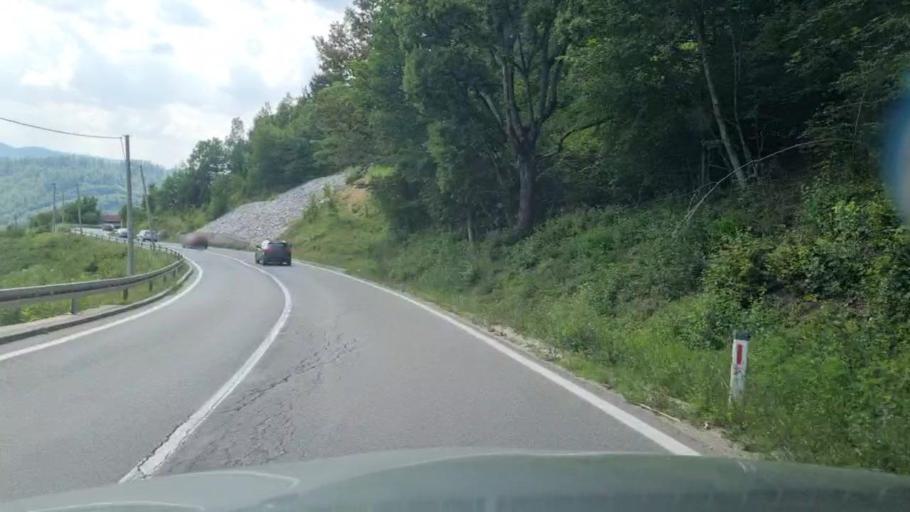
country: BA
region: Federation of Bosnia and Herzegovina
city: Kladanj
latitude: 44.2406
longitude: 18.7278
